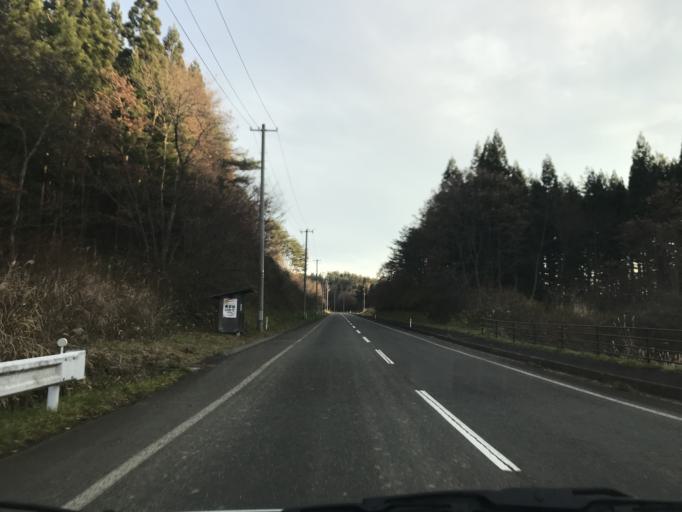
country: JP
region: Iwate
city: Ichinoseki
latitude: 38.9897
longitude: 141.0667
